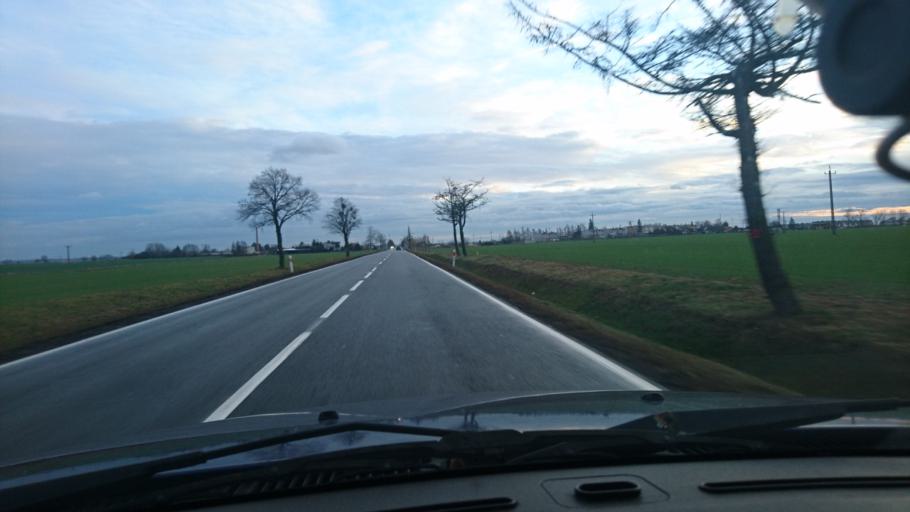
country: PL
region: Opole Voivodeship
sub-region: Powiat kluczborski
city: Kluczbork
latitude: 50.9997
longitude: 18.2064
